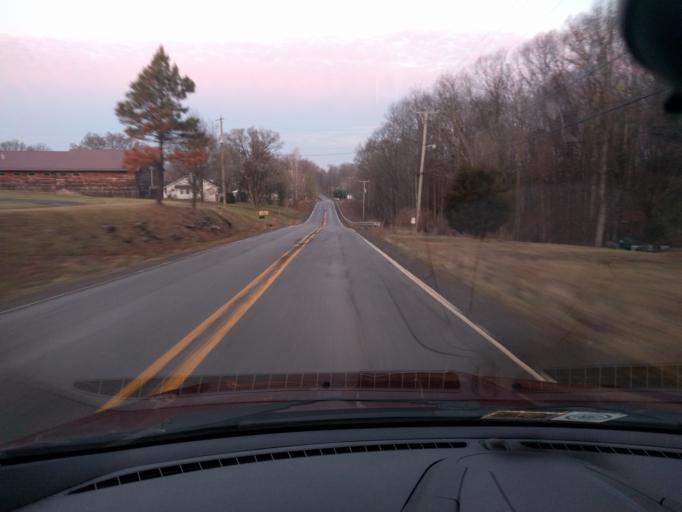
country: US
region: West Virginia
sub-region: Greenbrier County
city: Rainelle
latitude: 38.0132
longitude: -80.8963
